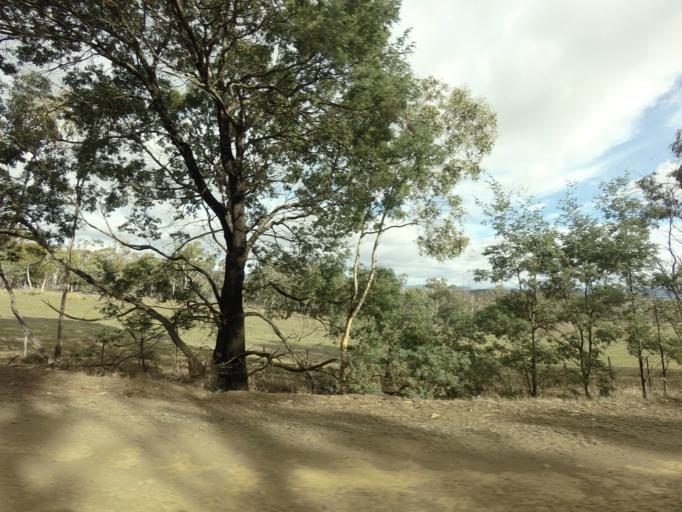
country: AU
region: Tasmania
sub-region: Brighton
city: Bridgewater
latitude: -42.4605
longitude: 147.2638
